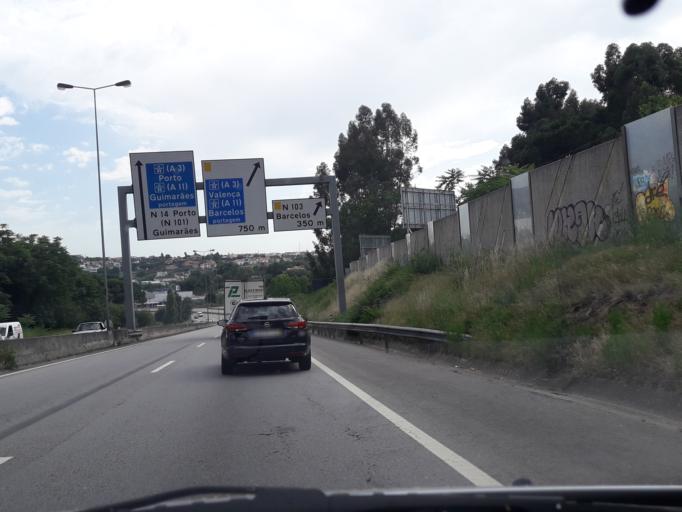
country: PT
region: Braga
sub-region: Braga
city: Braga
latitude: 41.5392
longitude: -8.4431
